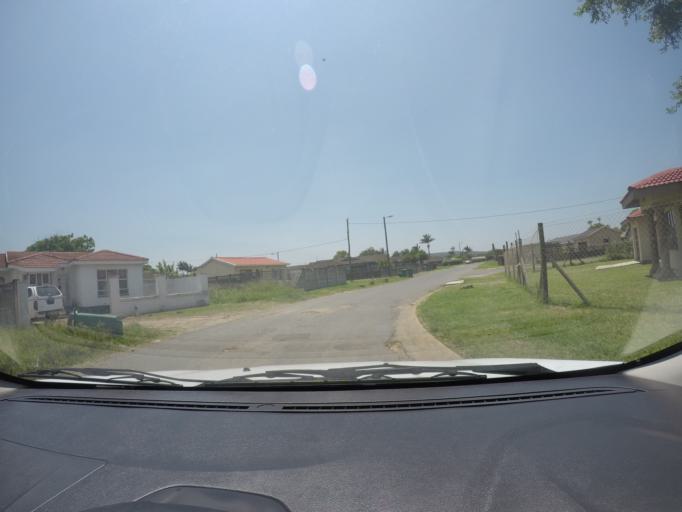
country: ZA
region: KwaZulu-Natal
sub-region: uThungulu District Municipality
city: eSikhawini
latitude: -28.8875
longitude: 31.8872
